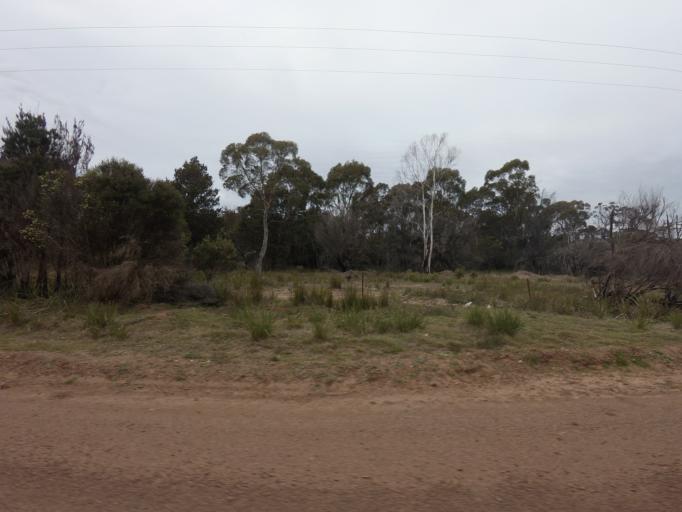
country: AU
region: Tasmania
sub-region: Break O'Day
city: St Helens
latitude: -41.9351
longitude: 148.0742
